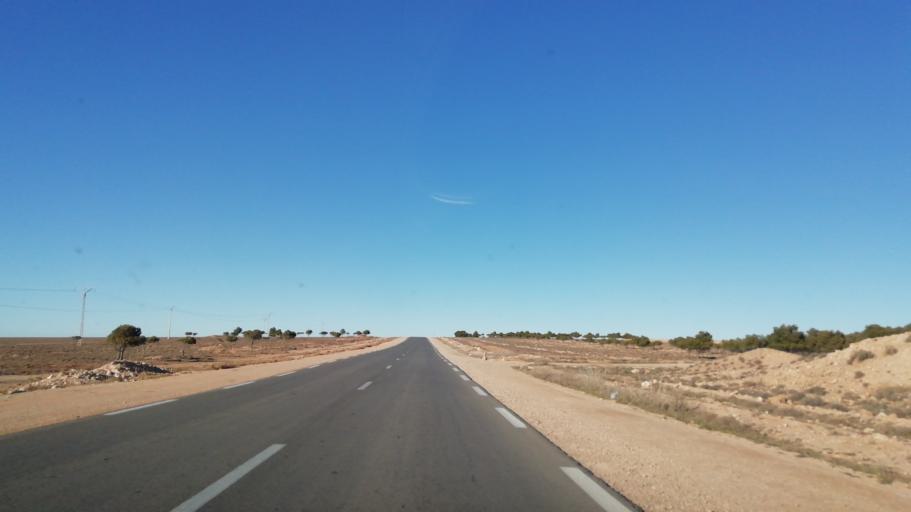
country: DZ
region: Tlemcen
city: Sebdou
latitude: 34.2552
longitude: -1.2576
